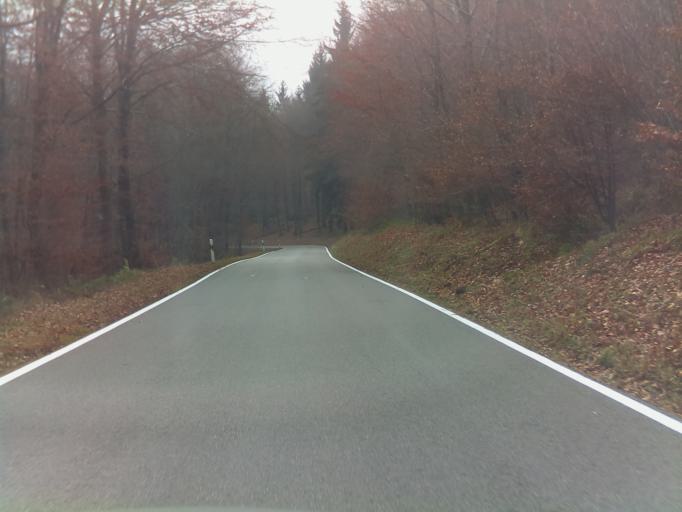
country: DE
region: Baden-Wuerttemberg
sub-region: Karlsruhe Region
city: Gaiberg
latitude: 49.3948
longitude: 8.7303
